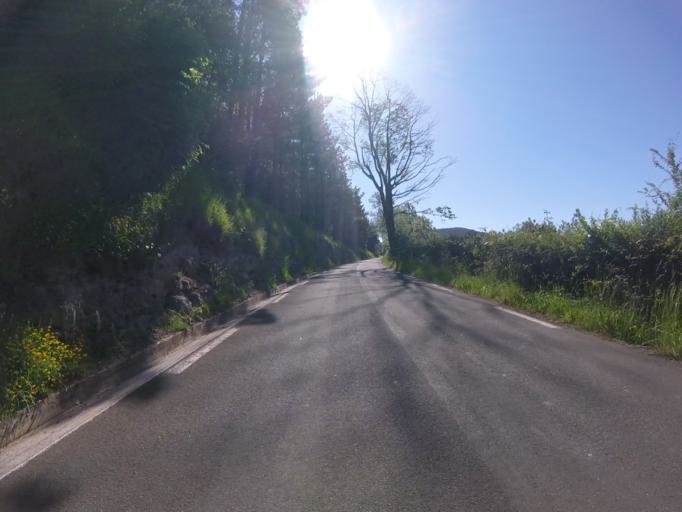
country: ES
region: Basque Country
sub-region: Provincia de Guipuzcoa
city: Beizama
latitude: 43.1244
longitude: -2.1928
